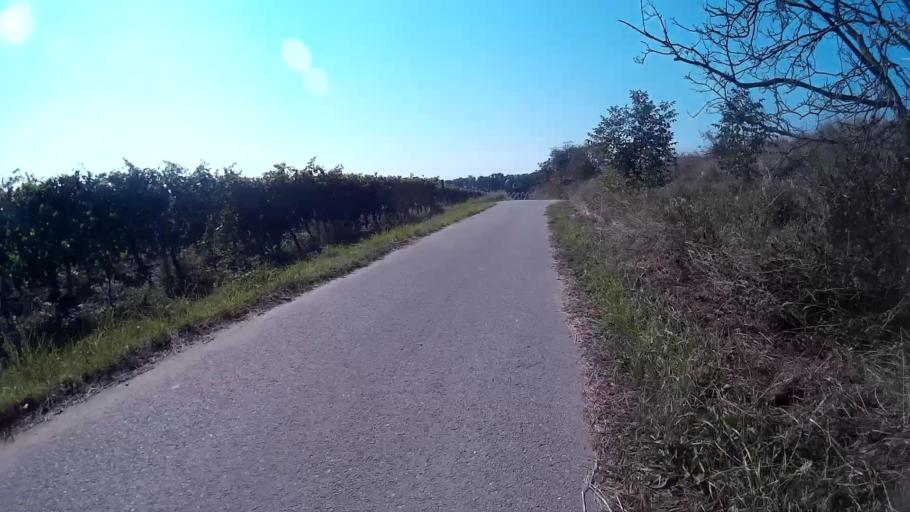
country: CZ
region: South Moravian
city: Novosedly
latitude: 48.8479
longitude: 16.5266
